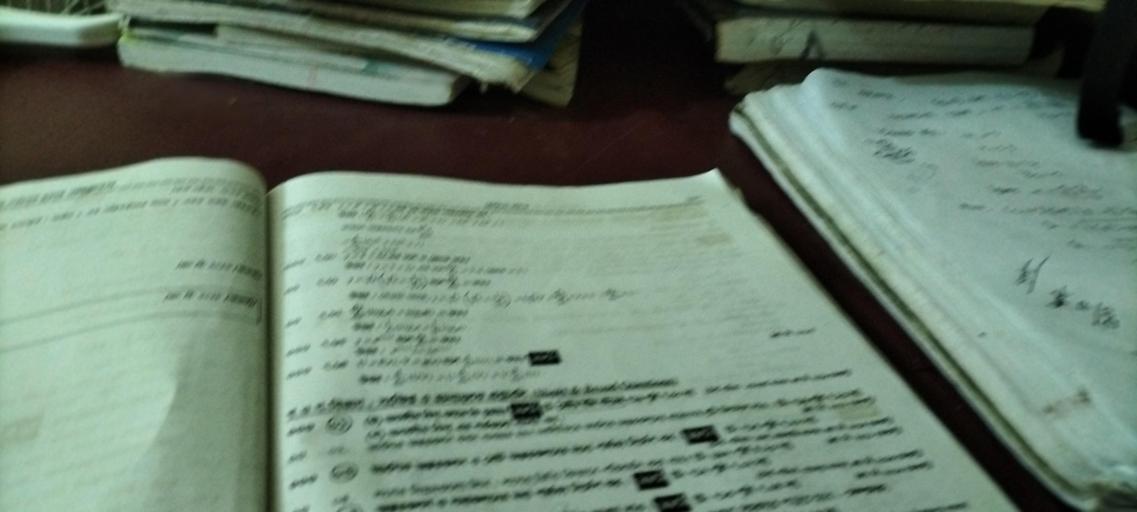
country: BD
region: Chittagong
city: Chittagong
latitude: 22.3538
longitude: 91.8503
